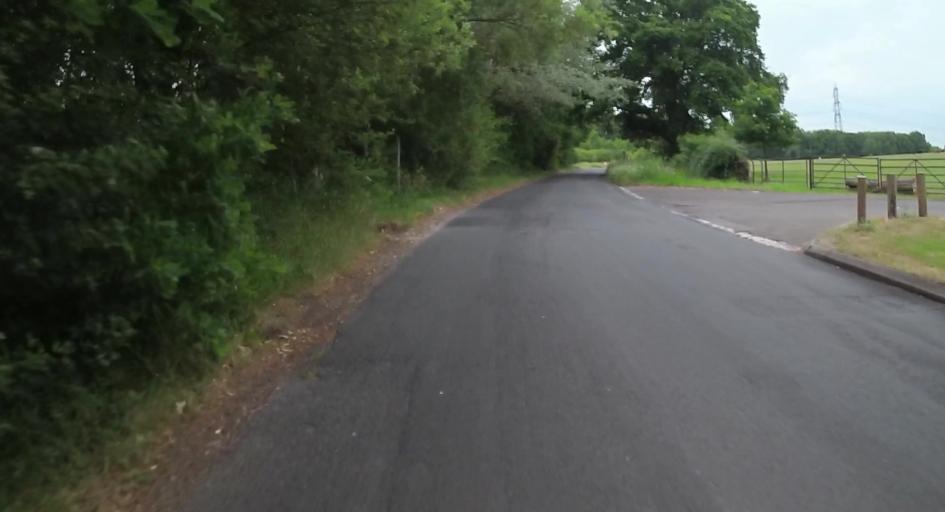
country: GB
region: England
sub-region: Hampshire
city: Odiham
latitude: 51.2566
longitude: -0.8892
